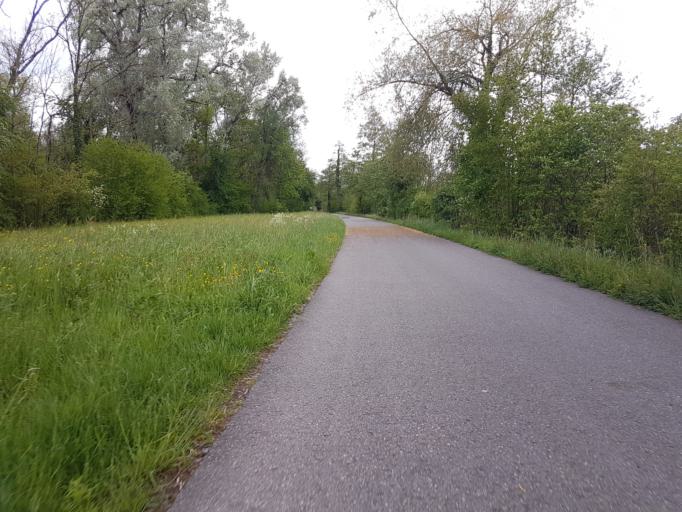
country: CH
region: Solothurn
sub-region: Bezirk Goesgen
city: Niedererlinsbach
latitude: 47.3923
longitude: 8.0226
